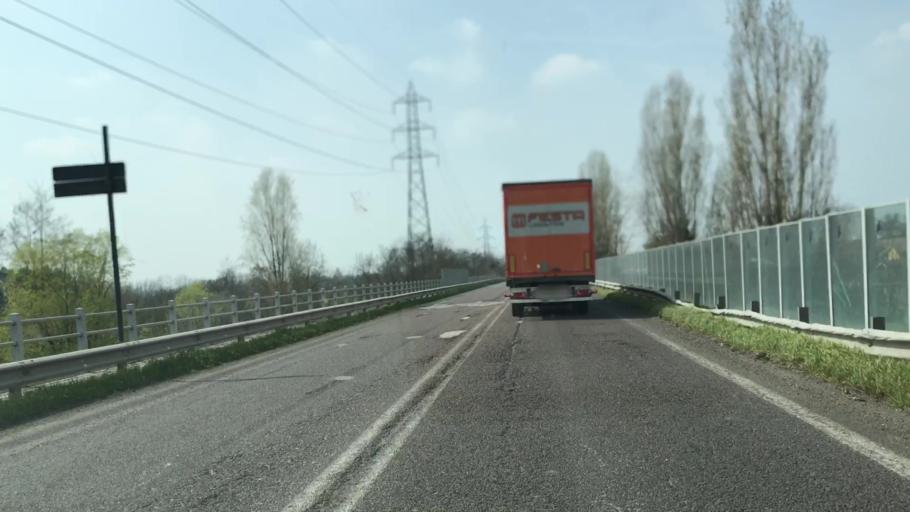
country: IT
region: Lombardy
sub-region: Provincia di Mantova
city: Sant'Antonio
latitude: 45.1858
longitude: 10.7824
